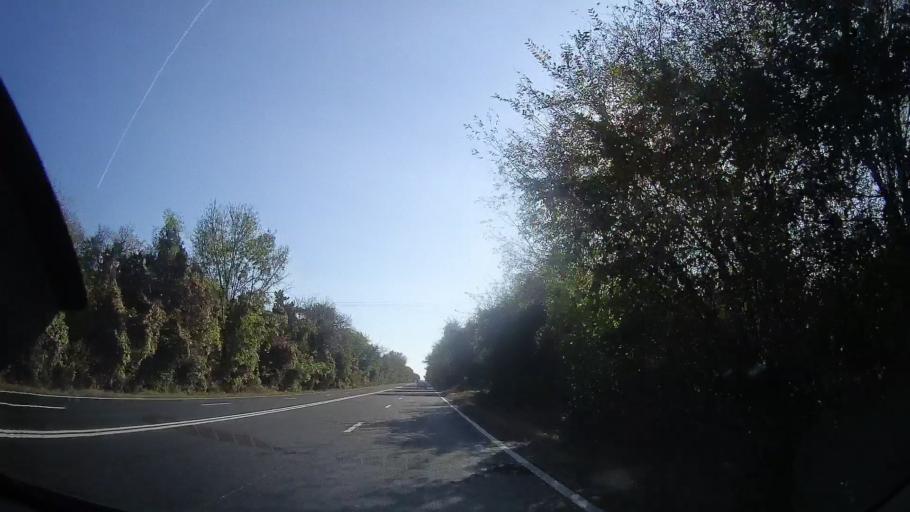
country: RO
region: Constanta
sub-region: Comuna Douazeci si Trei August
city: Dulcesti
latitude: 43.8682
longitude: 28.5747
